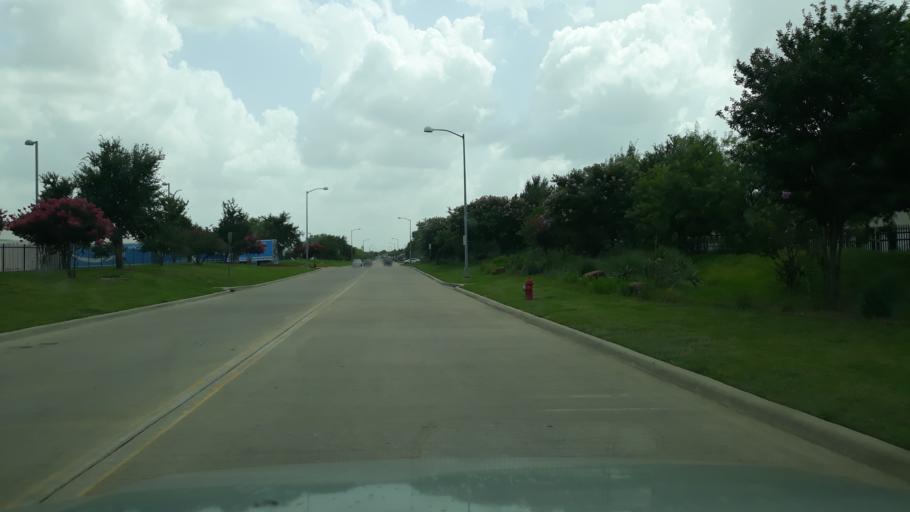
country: US
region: Texas
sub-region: Dallas County
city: Coppell
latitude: 32.9413
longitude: -97.0291
